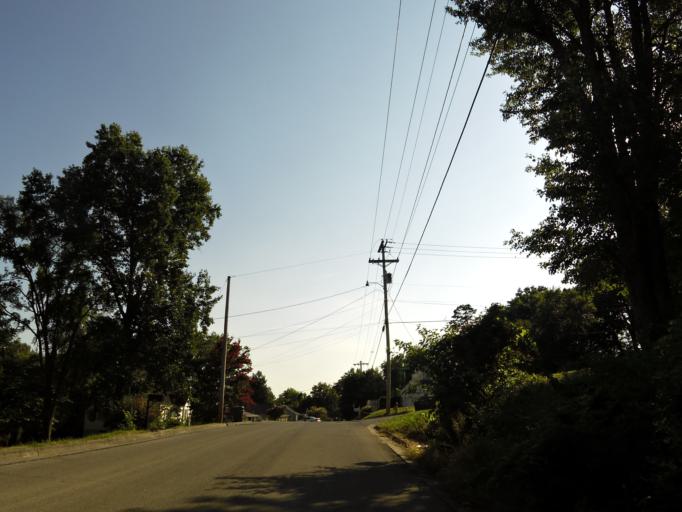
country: US
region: Tennessee
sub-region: Blount County
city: Maryville
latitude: 35.7641
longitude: -83.9579
